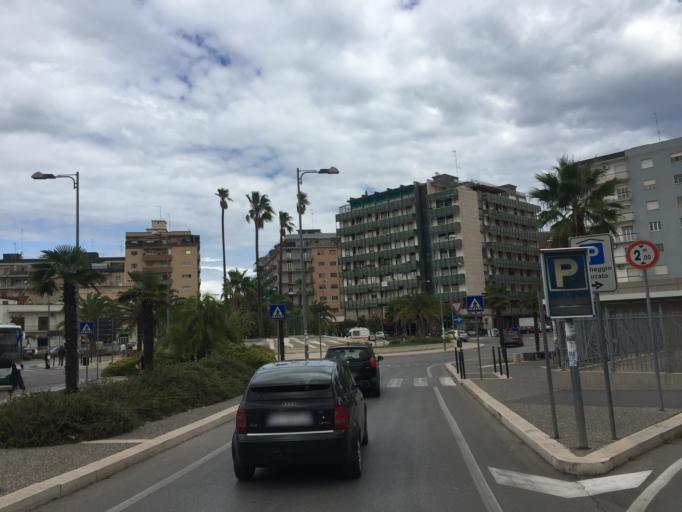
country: IT
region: Apulia
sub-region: Provincia di Bari
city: Bari
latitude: 41.1117
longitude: 16.8626
